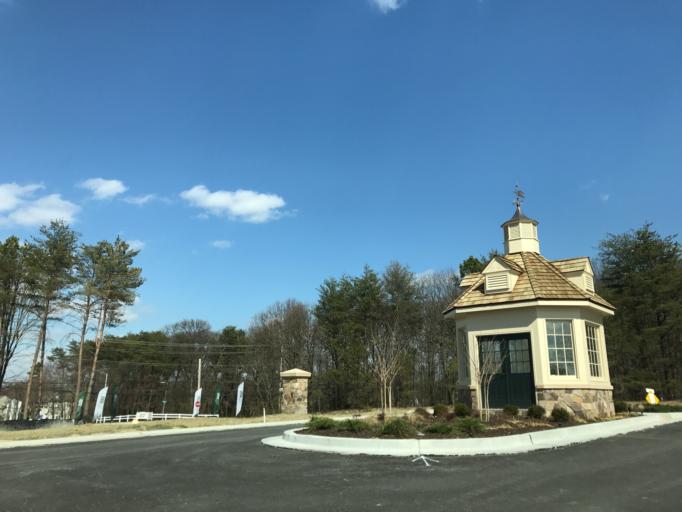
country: US
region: Maryland
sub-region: Anne Arundel County
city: Green Haven
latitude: 39.1291
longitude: -76.5552
